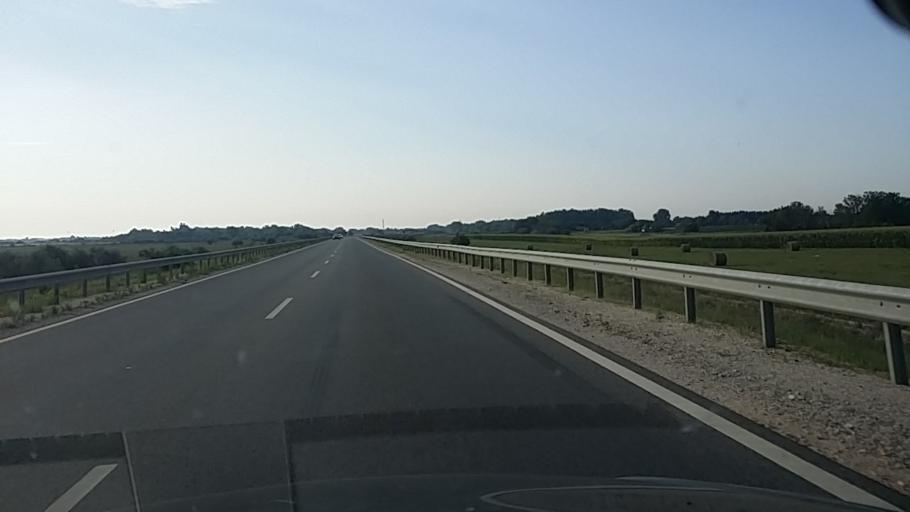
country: HU
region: Bacs-Kiskun
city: Kecskemet
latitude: 46.9259
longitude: 19.7182
